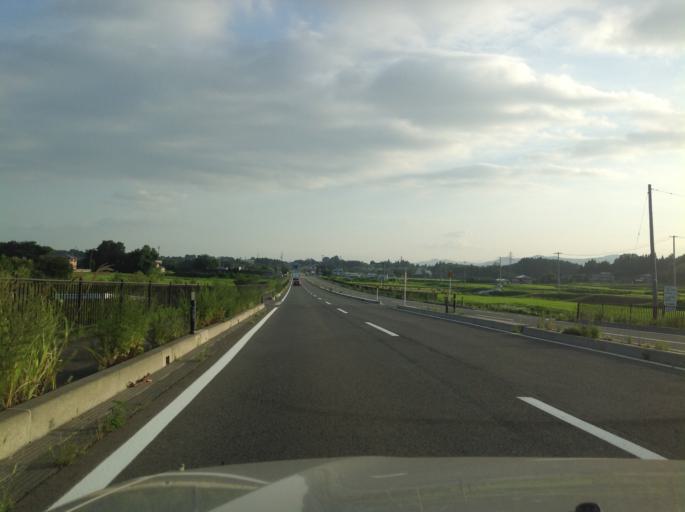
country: JP
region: Iwate
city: Hanamaki
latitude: 39.5073
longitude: 141.1501
